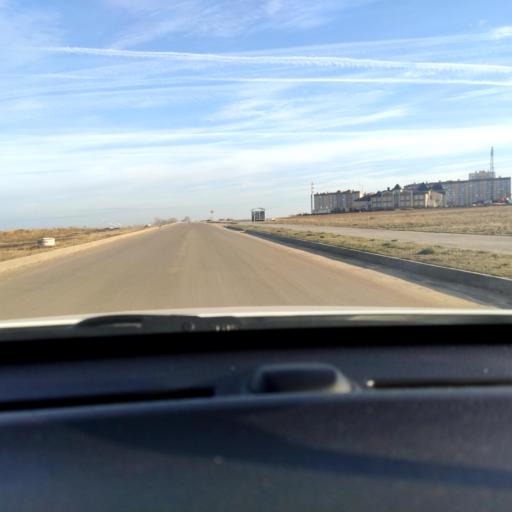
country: RU
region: Voronezj
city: Shilovo
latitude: 51.5727
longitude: 39.1187
